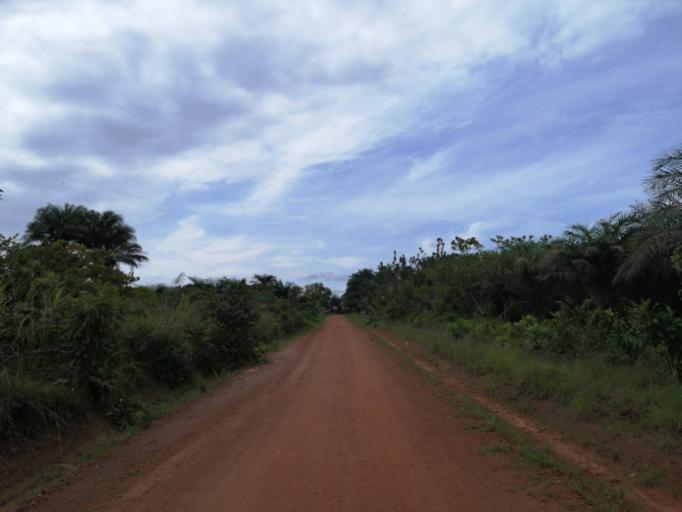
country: SL
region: Northern Province
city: Port Loko
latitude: 8.7680
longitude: -12.9058
